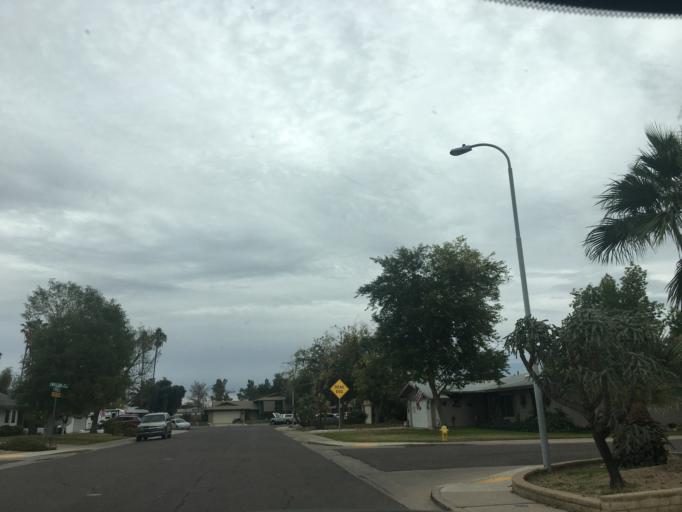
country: US
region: Arizona
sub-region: Maricopa County
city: Tempe
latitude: 33.3826
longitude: -111.9121
